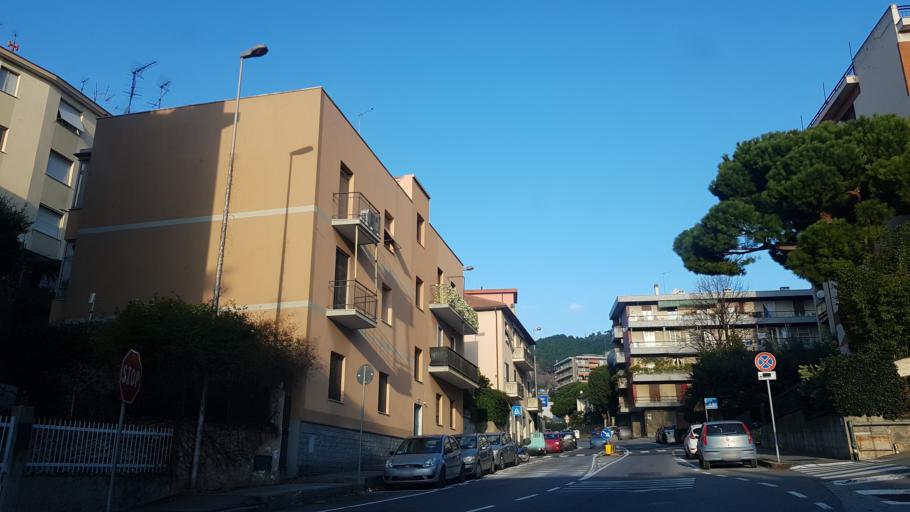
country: IT
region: Liguria
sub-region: Provincia di Savona
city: Savona
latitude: 44.3049
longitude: 8.4677
